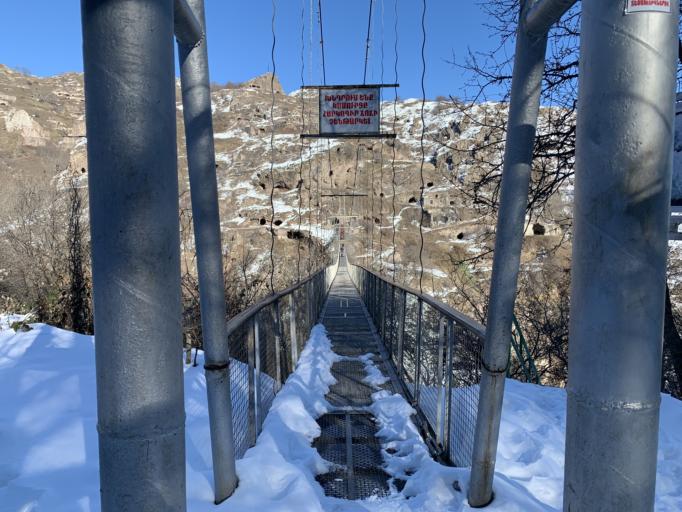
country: AM
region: Syunik'i Marz
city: Khndzoresk
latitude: 39.5003
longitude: 46.4322
